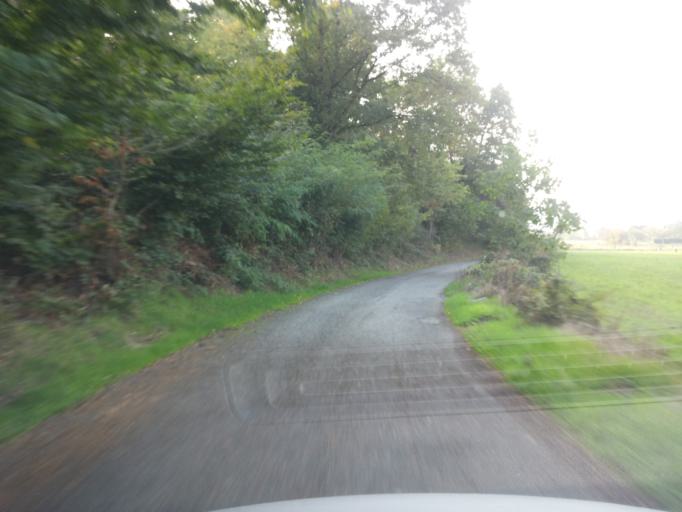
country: IT
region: Piedmont
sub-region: Provincia di Biella
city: Viverone
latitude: 45.3994
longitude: 8.0486
